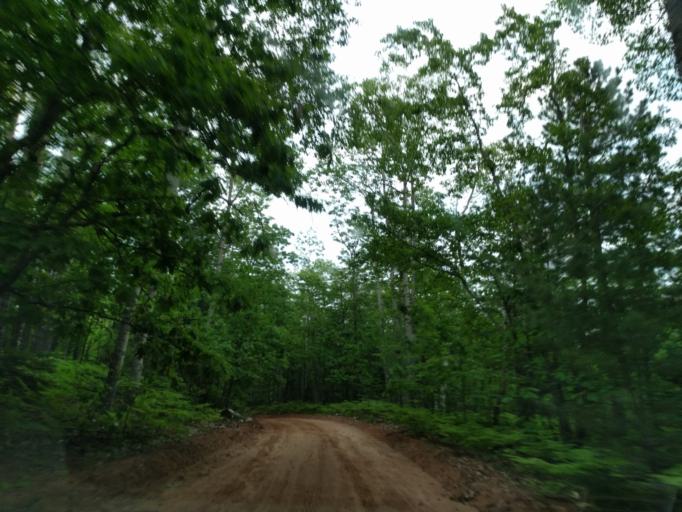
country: US
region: Michigan
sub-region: Marquette County
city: Trowbridge Park
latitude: 46.6171
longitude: -87.5065
